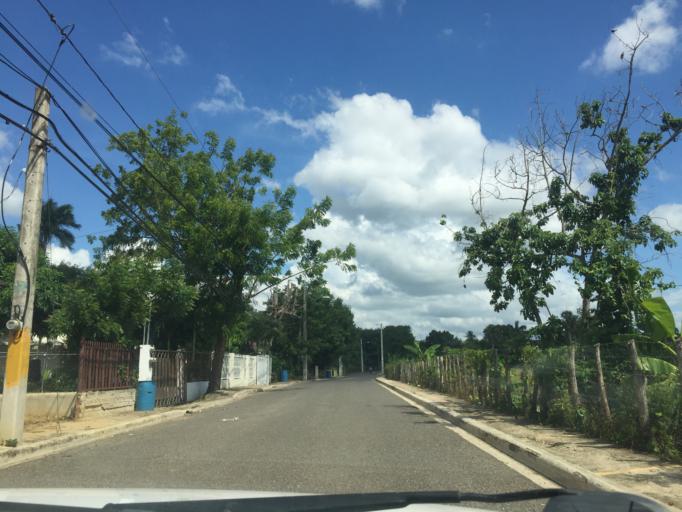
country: DO
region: Santiago
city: Licey al Medio
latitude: 19.3813
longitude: -70.6027
